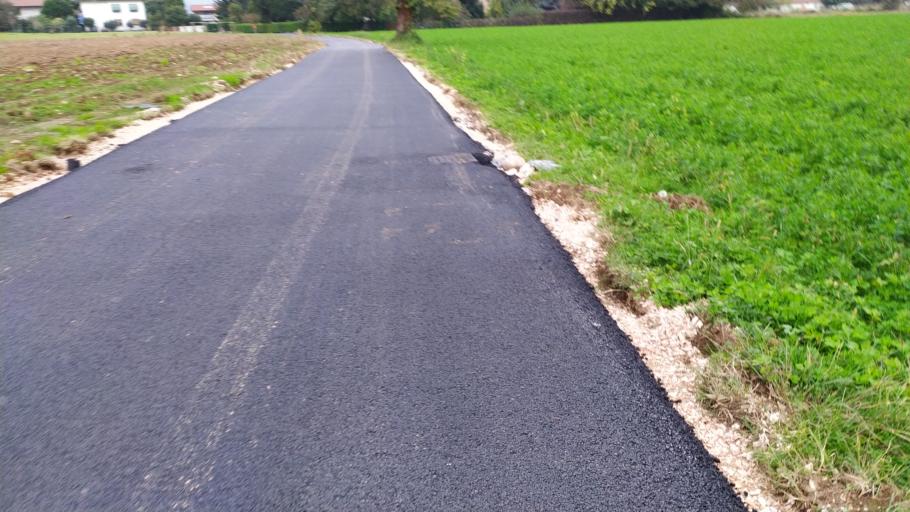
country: IT
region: Veneto
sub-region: Provincia di Vicenza
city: Schio
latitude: 45.7002
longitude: 11.3690
